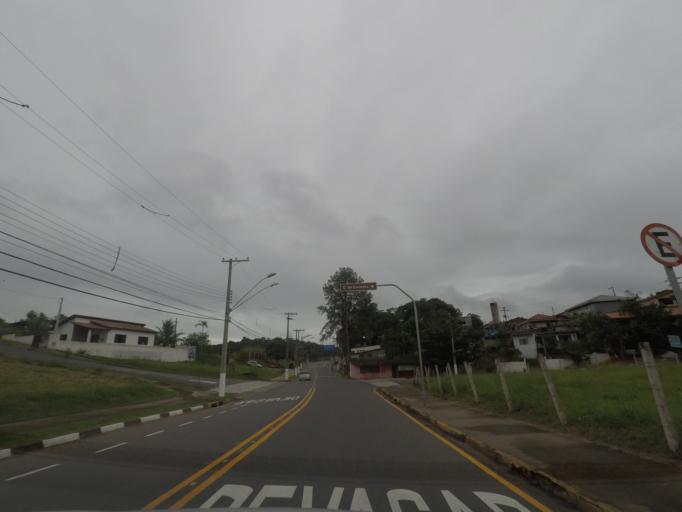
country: BR
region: Sao Paulo
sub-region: Cajati
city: Cajati
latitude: -24.7219
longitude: -48.1027
